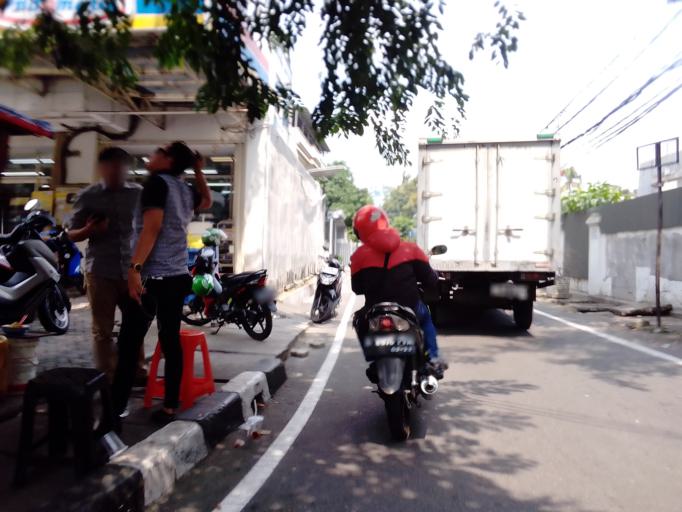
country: ID
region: Jakarta Raya
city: Jakarta
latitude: -6.1762
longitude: 106.8099
